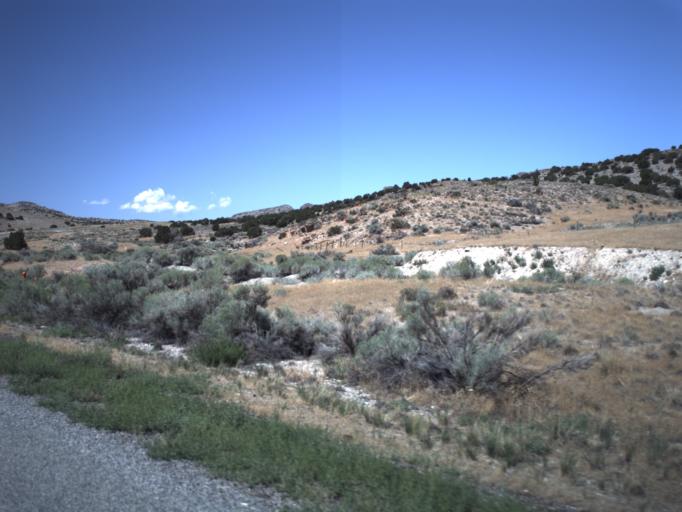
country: US
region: Utah
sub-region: Beaver County
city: Milford
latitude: 39.0807
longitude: -113.6054
